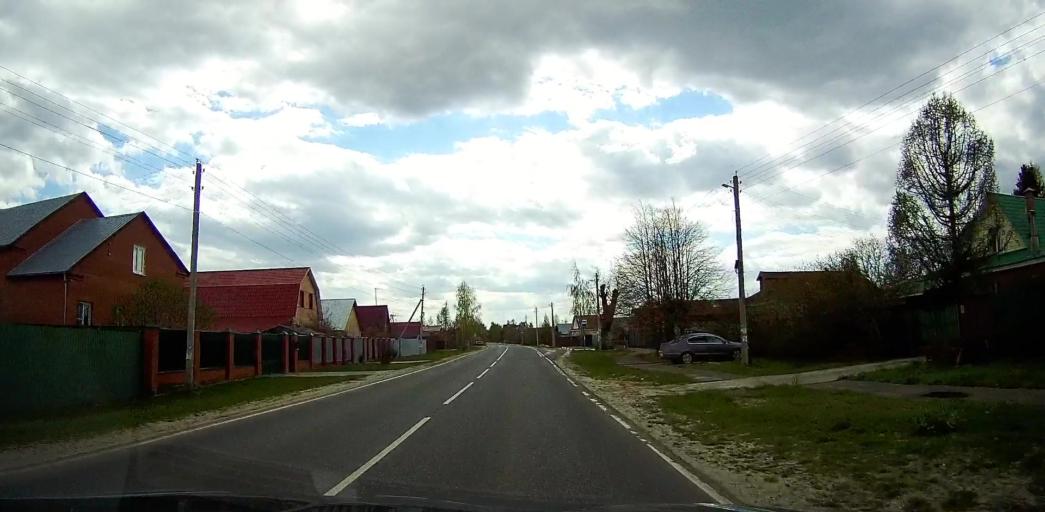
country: RU
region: Moskovskaya
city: Davydovo
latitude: 55.6653
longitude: 38.7596
